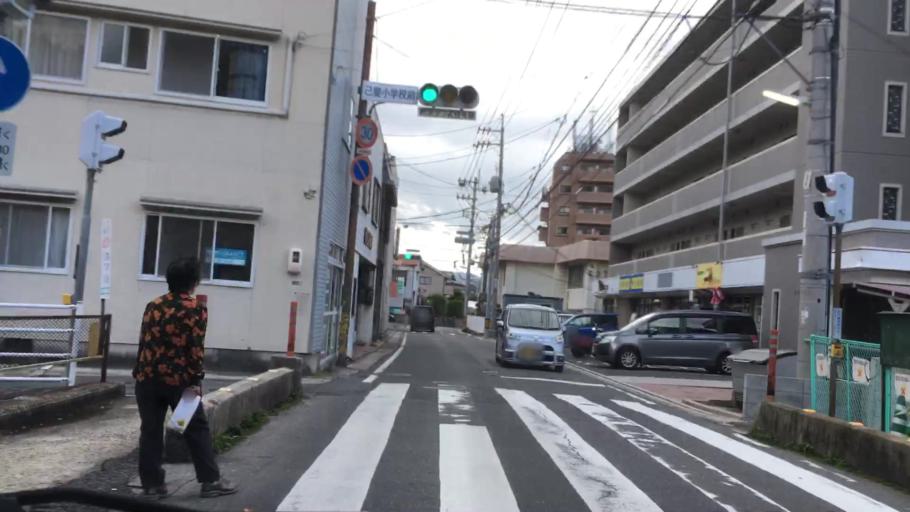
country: JP
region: Hiroshima
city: Hiroshima-shi
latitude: 34.4008
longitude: 132.4226
